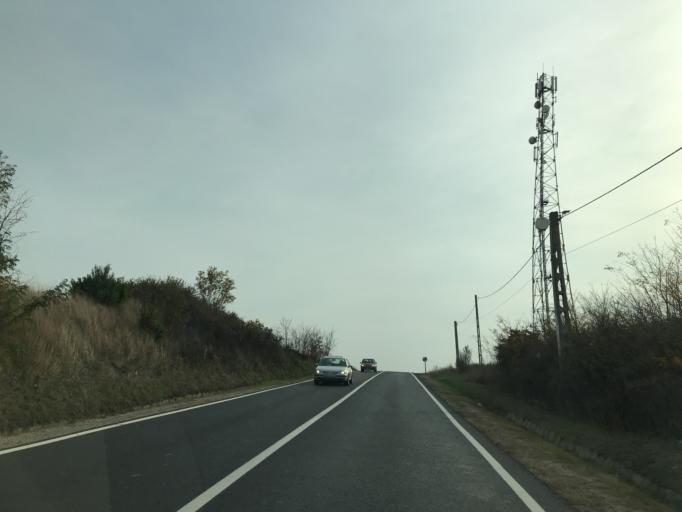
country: RO
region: Olt
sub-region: Comuna Piatra Olt
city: Piatra
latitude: 44.3498
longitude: 24.2955
